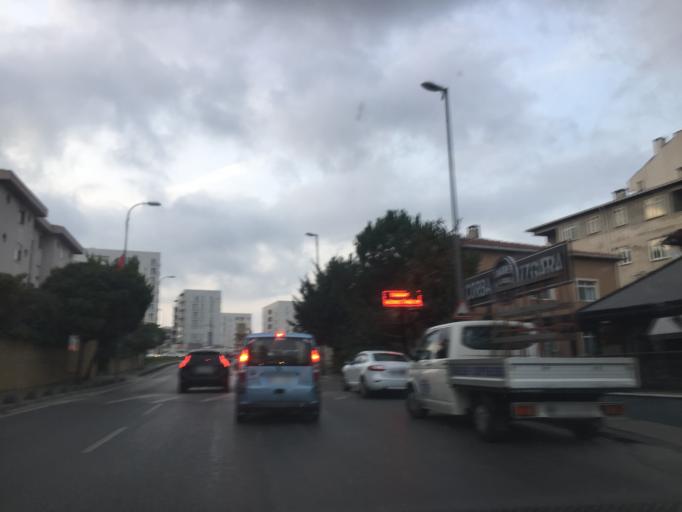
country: TR
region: Istanbul
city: Samandira
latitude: 40.9895
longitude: 29.2301
